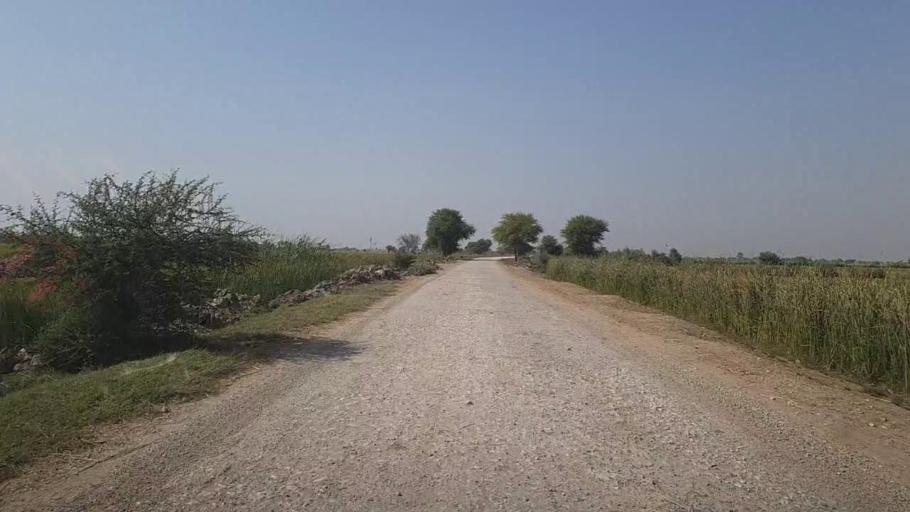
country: PK
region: Sindh
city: Kandhkot
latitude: 28.3947
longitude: 69.2751
